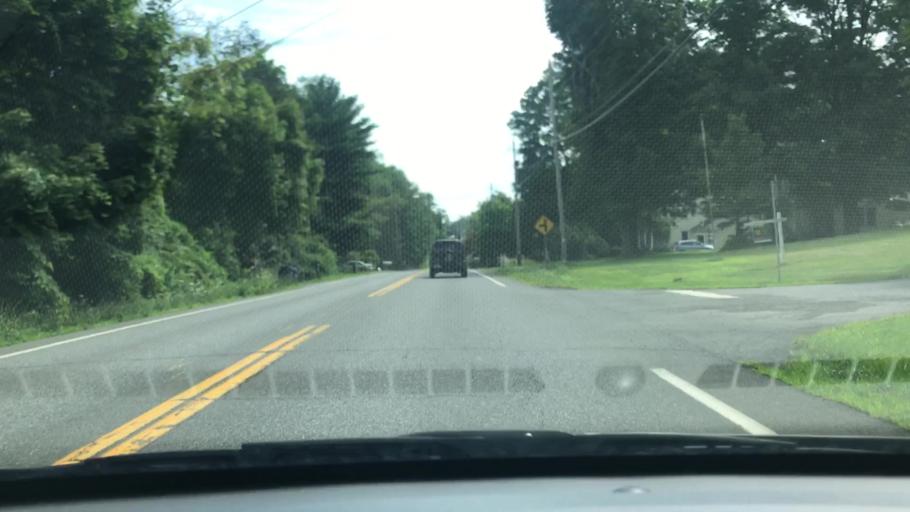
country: US
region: New York
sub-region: Ulster County
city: Shokan
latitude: 41.9730
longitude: -74.2223
